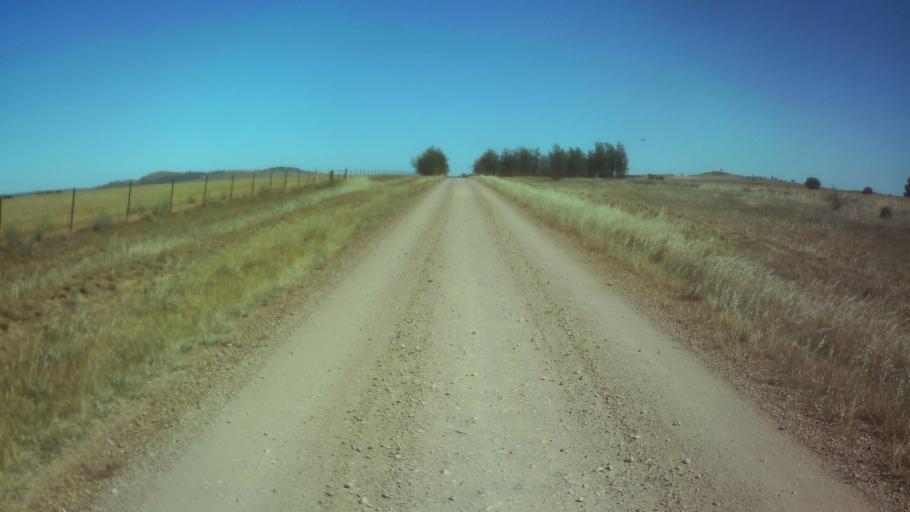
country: AU
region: New South Wales
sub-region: Weddin
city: Grenfell
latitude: -33.9853
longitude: 148.3331
